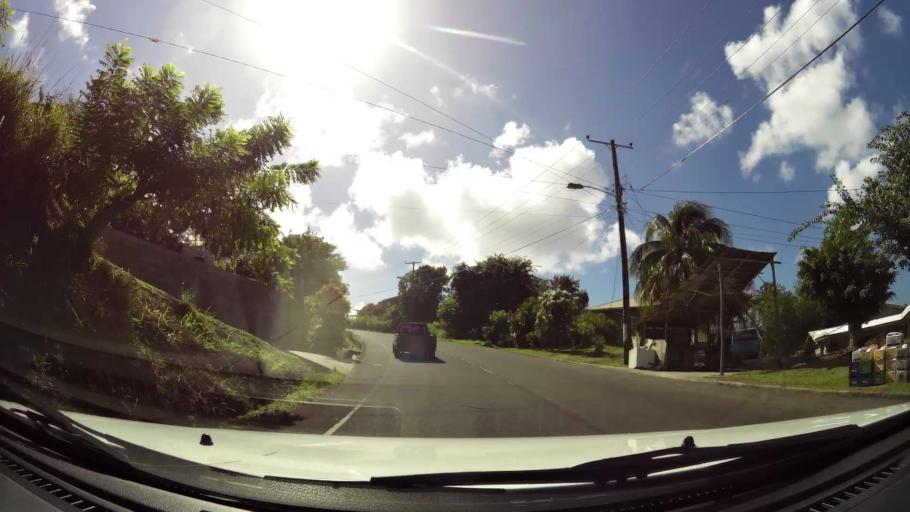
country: LC
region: Choiseul Quarter
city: Choiseul
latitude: 13.7642
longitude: -61.0335
